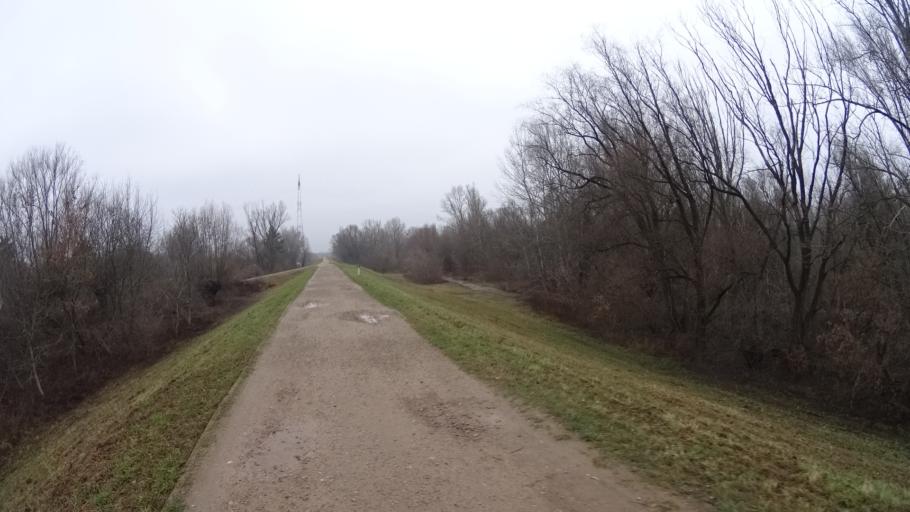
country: PL
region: Masovian Voivodeship
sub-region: Warszawa
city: Wilanow
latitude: 52.1942
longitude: 21.1011
